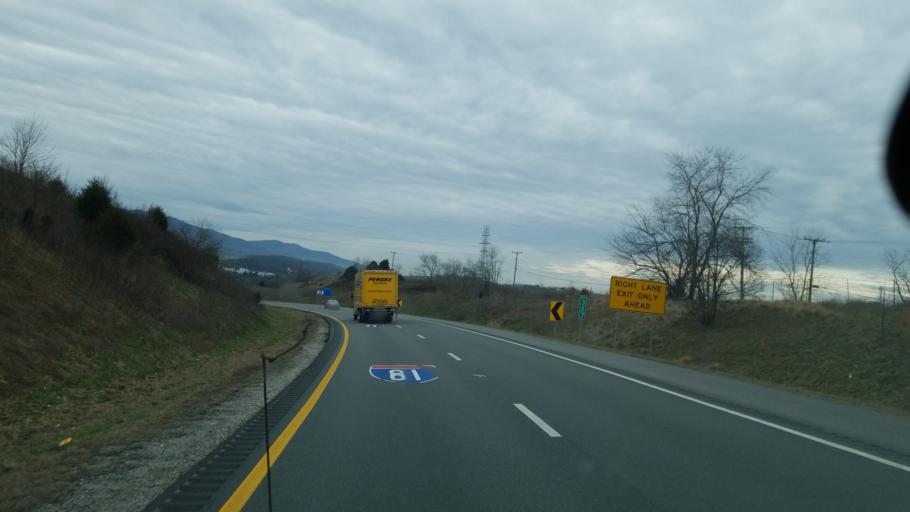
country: US
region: Virginia
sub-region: Wythe County
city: Wytheville
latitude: 36.9512
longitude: -80.9267
